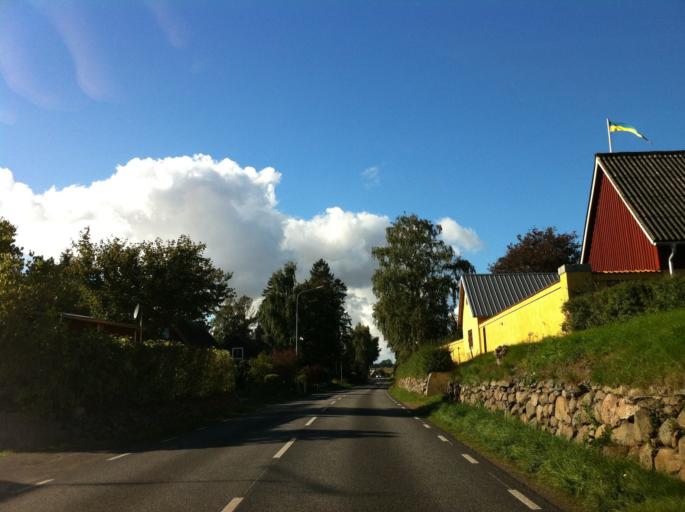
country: SE
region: Skane
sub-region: Hoors Kommun
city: Loberod
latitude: 55.7458
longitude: 13.4039
